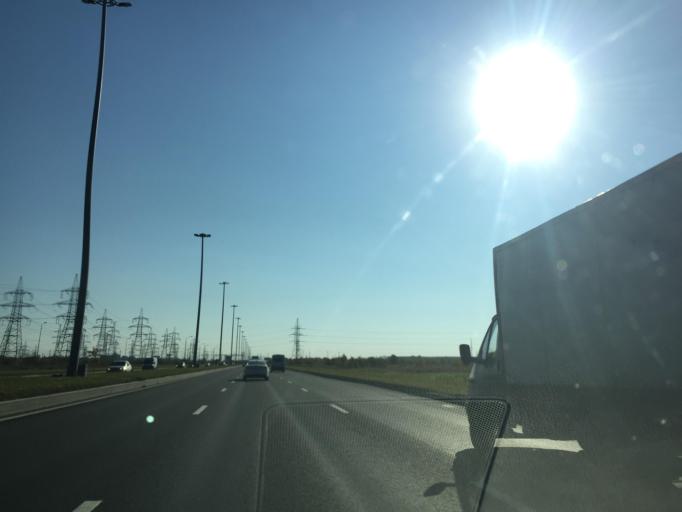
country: RU
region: St.-Petersburg
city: Petro-Slavyanka
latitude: 59.7566
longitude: 30.5178
